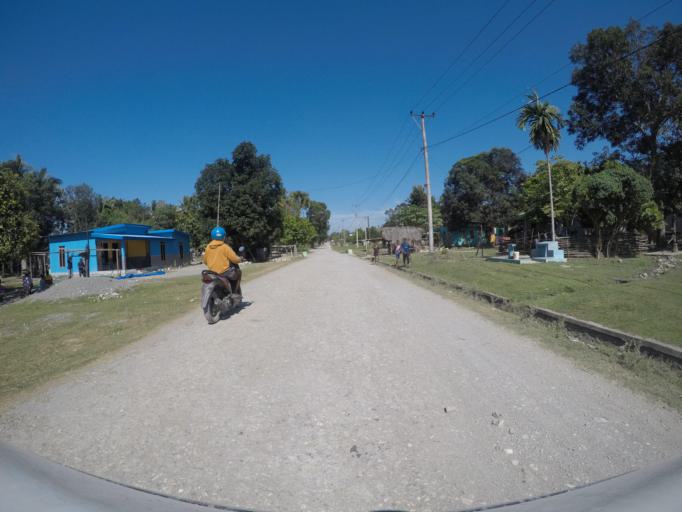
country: TL
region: Viqueque
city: Viqueque
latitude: -8.9756
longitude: 126.0478
